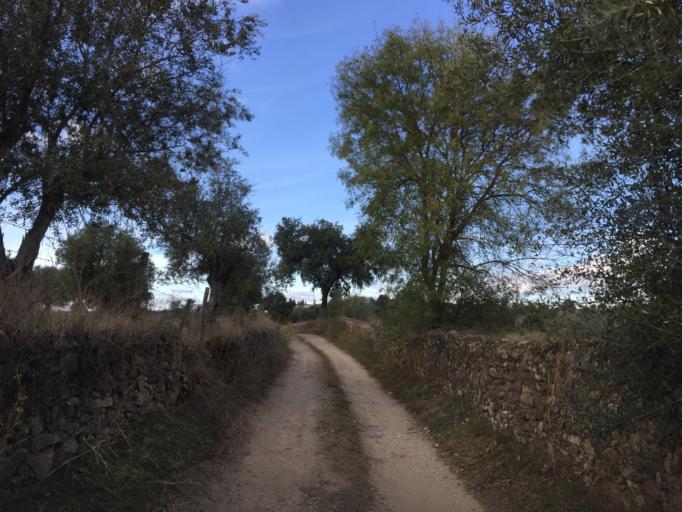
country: PT
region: Portalegre
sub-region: Alter do Chao
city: Alter do Chao
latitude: 39.2725
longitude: -7.6410
